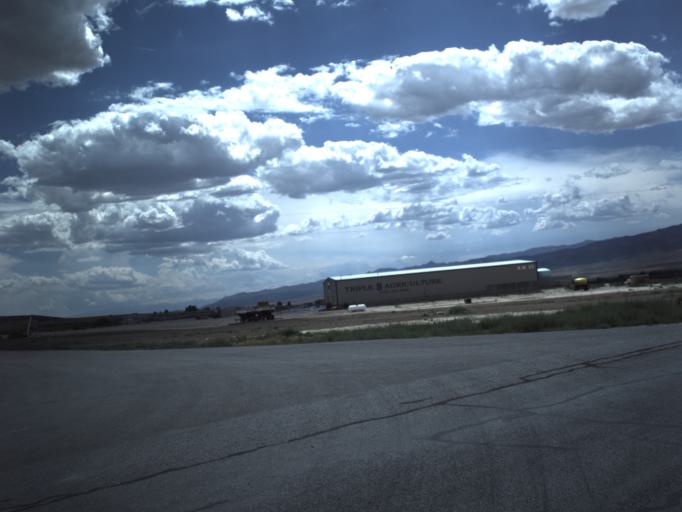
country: US
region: Utah
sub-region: Sanpete County
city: Centerfield
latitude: 39.1356
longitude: -111.7773
